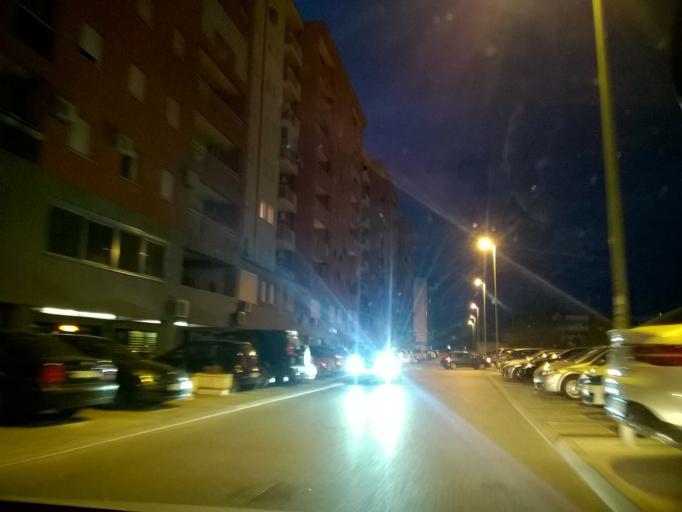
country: ME
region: Podgorica
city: Podgorica
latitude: 42.4401
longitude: 19.2373
